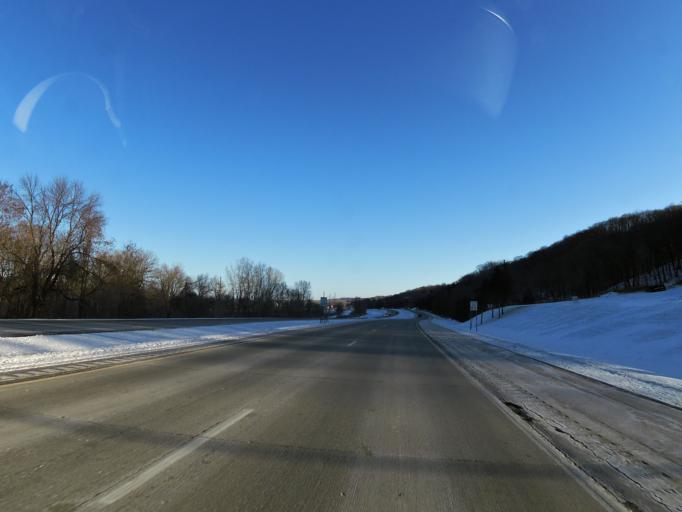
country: US
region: Minnesota
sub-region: Scott County
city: Jordan
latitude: 44.6897
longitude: -93.6073
